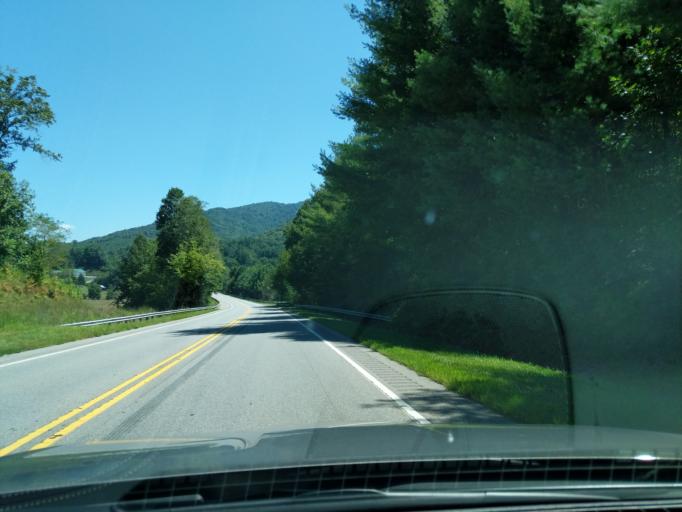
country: US
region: North Carolina
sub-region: Macon County
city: Franklin
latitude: 35.1378
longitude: -83.4931
